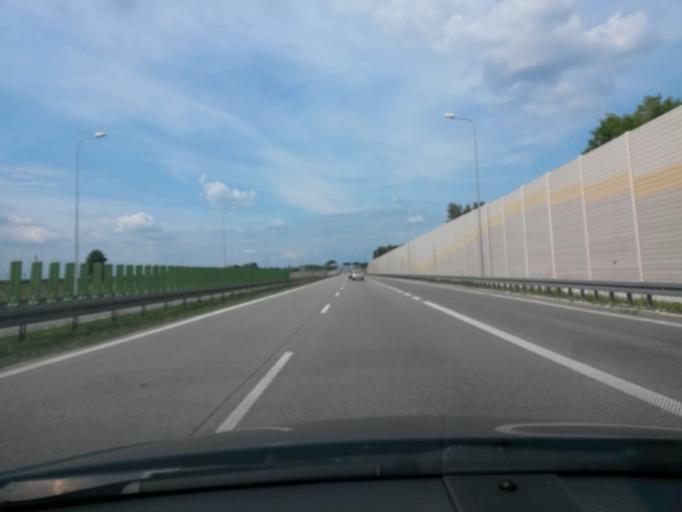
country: PL
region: Lodz Voivodeship
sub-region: Powiat skierniewicki
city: Kowiesy
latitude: 51.8923
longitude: 20.4232
